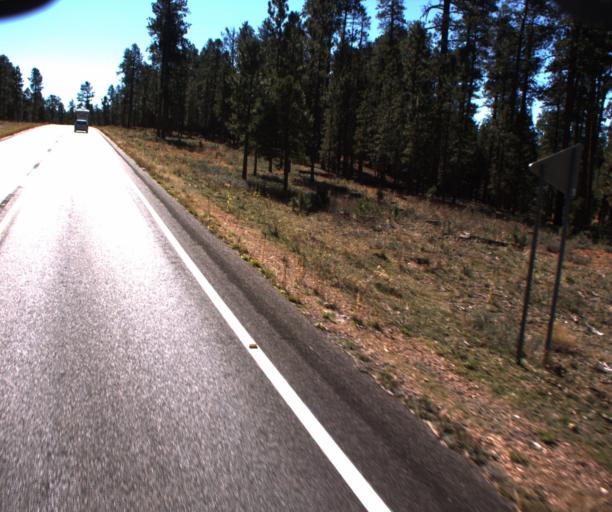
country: US
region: Arizona
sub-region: Coconino County
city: Fredonia
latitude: 36.6749
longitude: -112.2089
